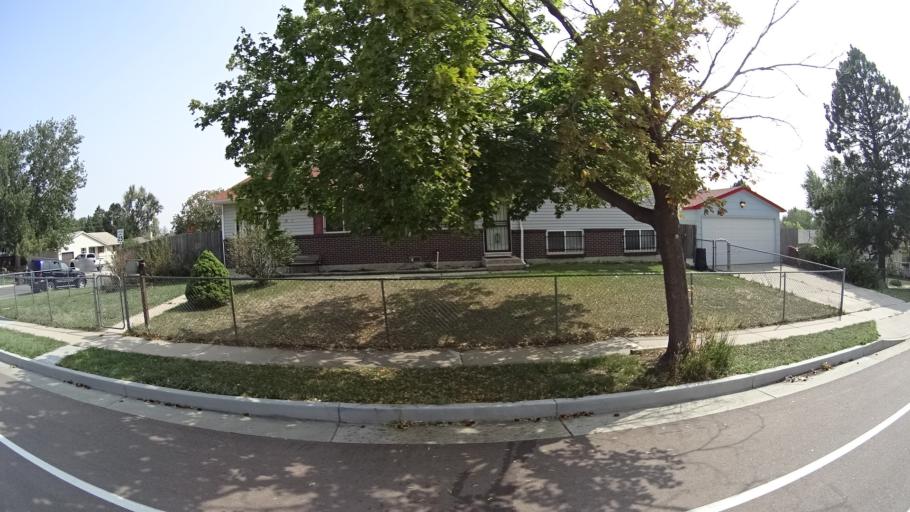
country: US
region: Colorado
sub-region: El Paso County
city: Stratmoor
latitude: 38.8050
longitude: -104.7715
